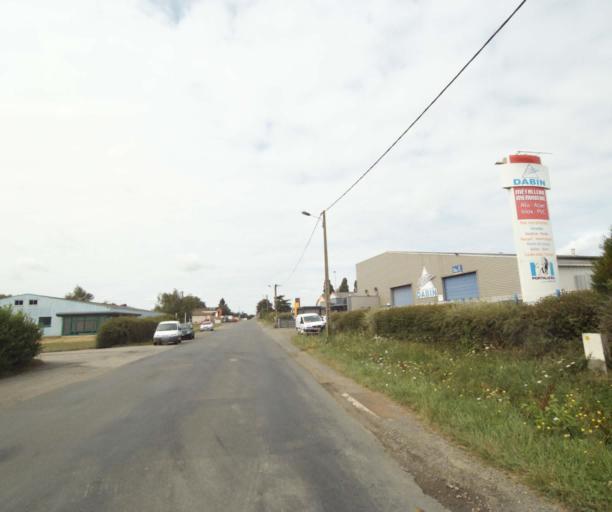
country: FR
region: Pays de la Loire
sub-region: Departement de la Sarthe
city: Solesmes
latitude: 47.8236
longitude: -0.3041
